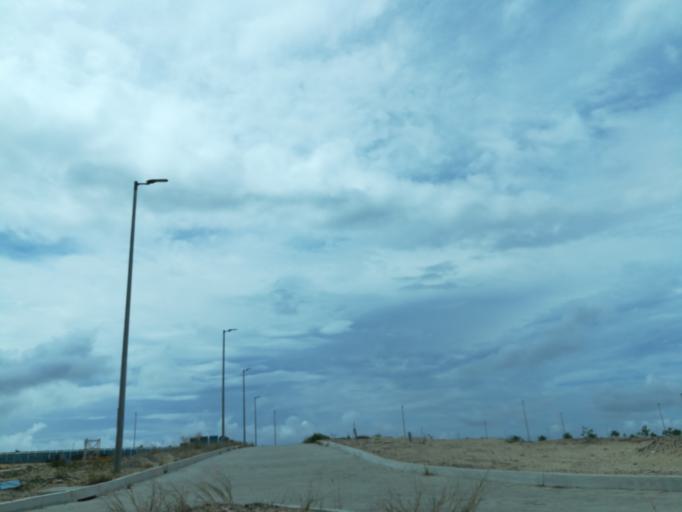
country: NG
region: Lagos
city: Lagos
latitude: 6.4121
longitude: 3.4136
